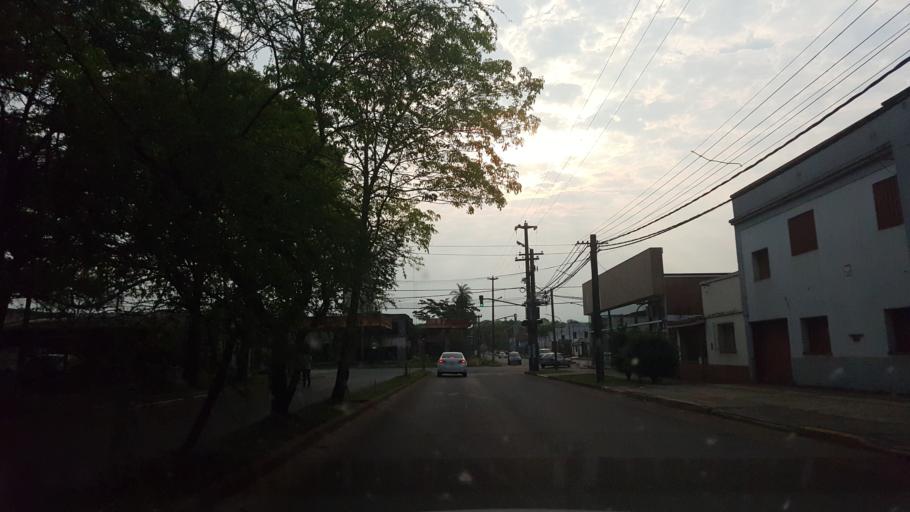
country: AR
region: Misiones
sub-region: Departamento de Capital
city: Posadas
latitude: -27.3979
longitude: -55.9011
